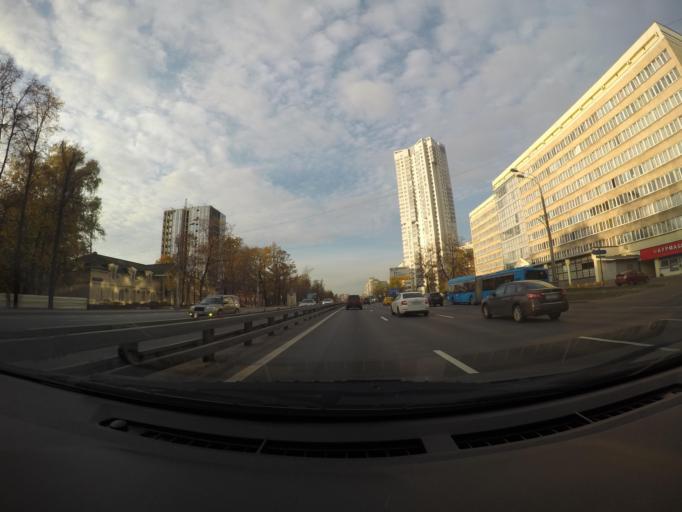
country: RU
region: Moskovskaya
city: Levoberezhnyy
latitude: 55.8585
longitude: 37.4680
